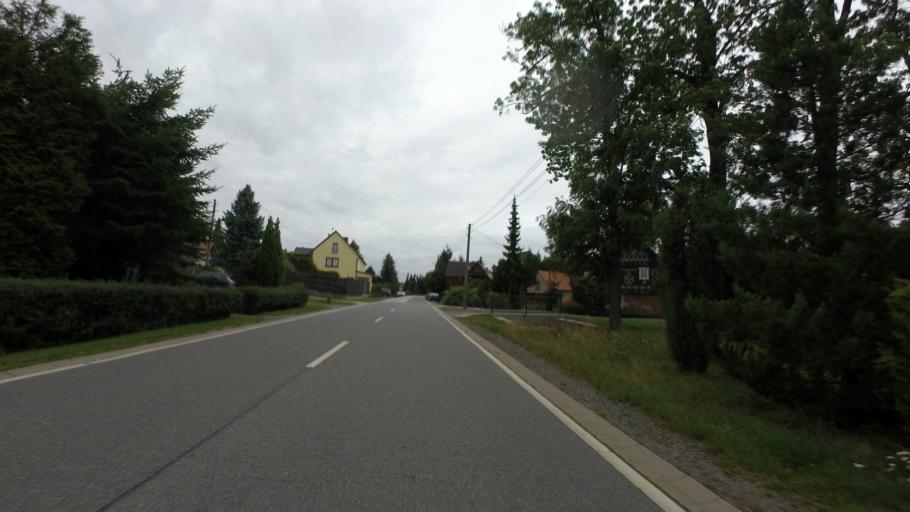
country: DE
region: Saxony
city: Berthelsdorf
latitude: 51.0606
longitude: 14.2245
